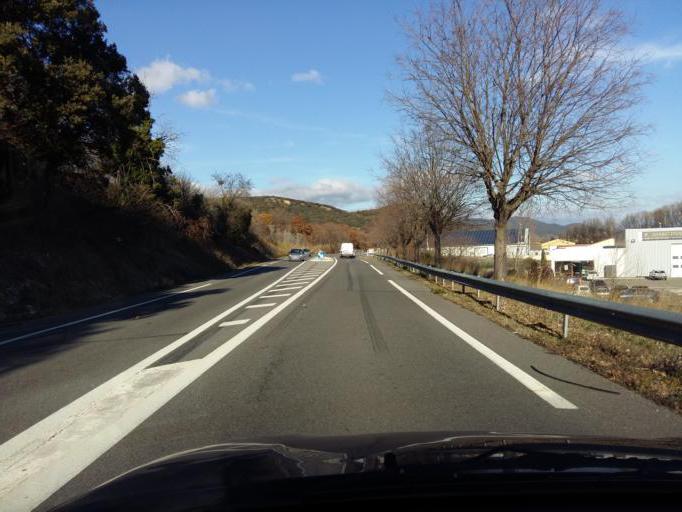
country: FR
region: Rhone-Alpes
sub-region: Departement de l'Ardeche
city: Bourg-Saint-Andeol
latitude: 44.3968
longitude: 4.6443
